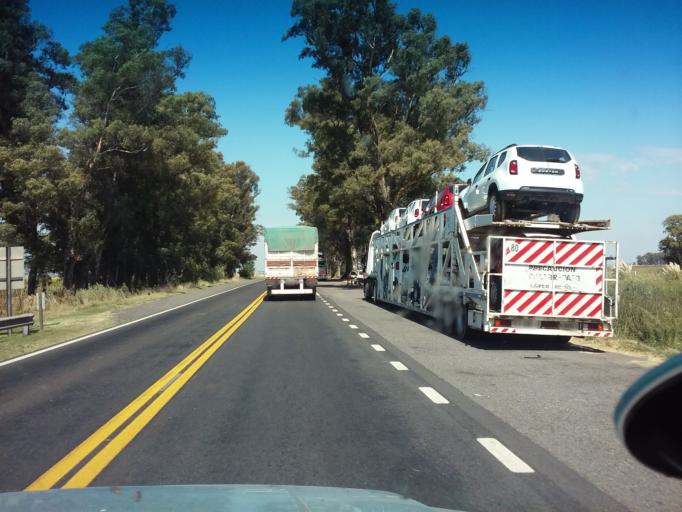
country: AR
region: Buenos Aires
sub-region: Partido de Nueve de Julio
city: Nueve de Julio
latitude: -35.3622
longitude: -60.7049
